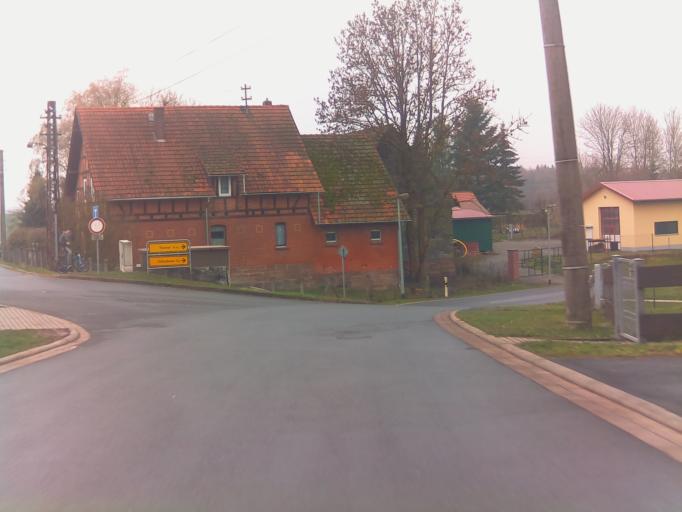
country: DE
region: Thuringia
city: Ehrenberg
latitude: 50.4801
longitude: 10.6570
